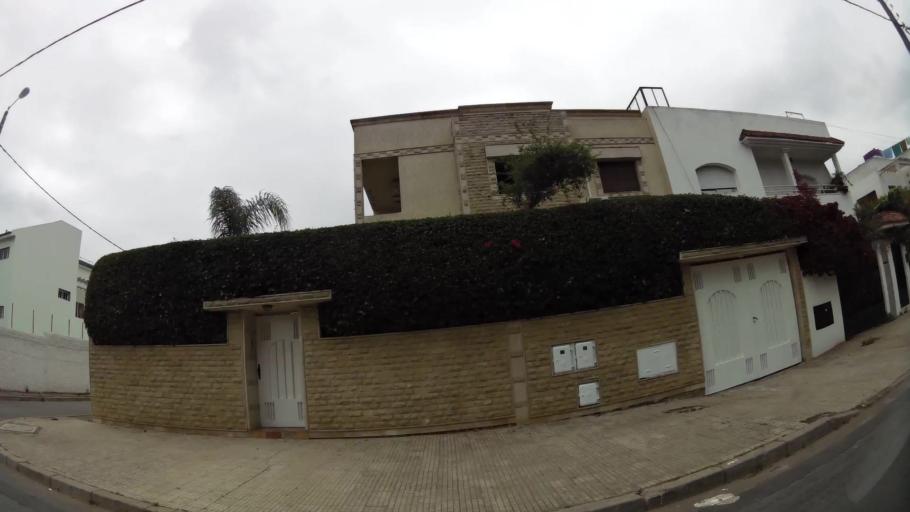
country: MA
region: Rabat-Sale-Zemmour-Zaer
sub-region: Rabat
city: Rabat
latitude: 33.9702
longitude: -6.8221
